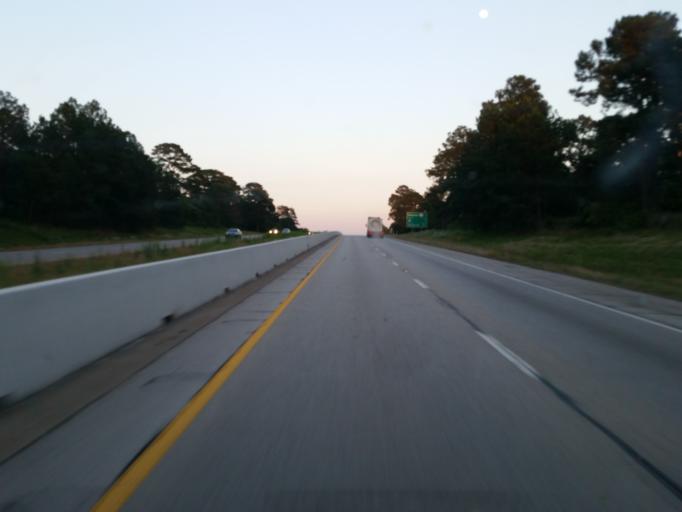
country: US
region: Texas
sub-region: Smith County
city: Hideaway
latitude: 32.4746
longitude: -95.4743
